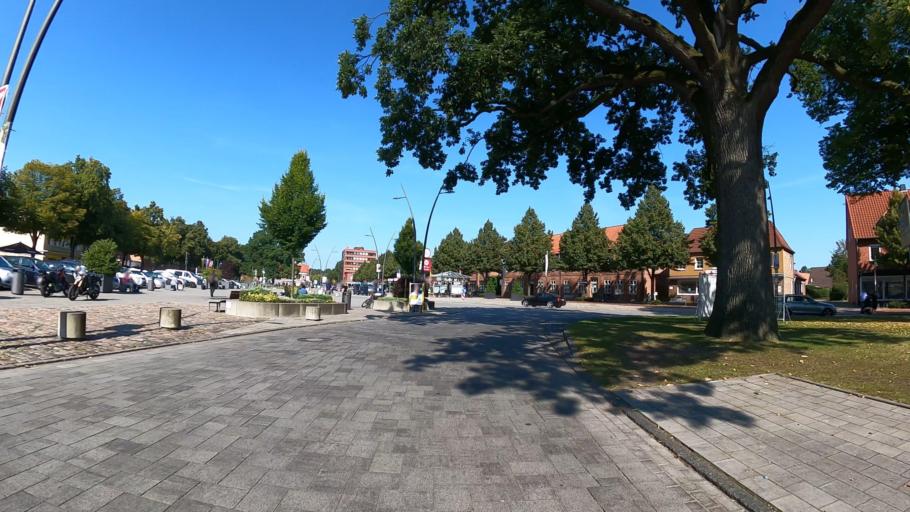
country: DE
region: Schleswig-Holstein
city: Bad Bramstedt
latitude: 53.9169
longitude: 9.8829
